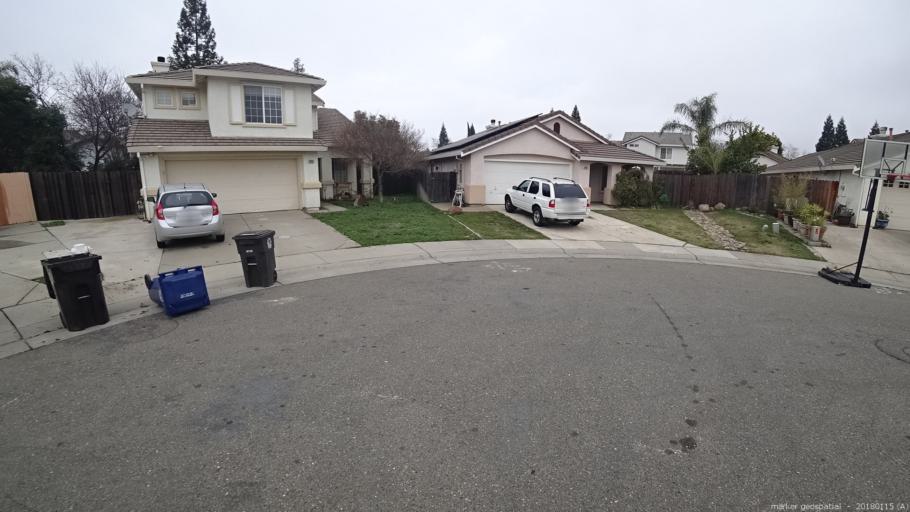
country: US
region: California
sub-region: Sacramento County
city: Rancho Cordova
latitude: 38.5799
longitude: -121.2923
